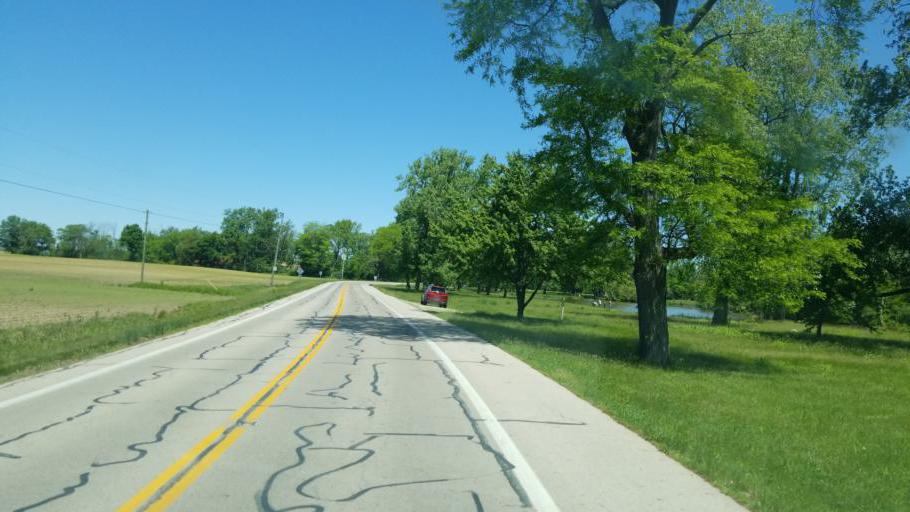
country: US
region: Ohio
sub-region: Auglaize County
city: Minster
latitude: 40.3791
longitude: -84.3587
